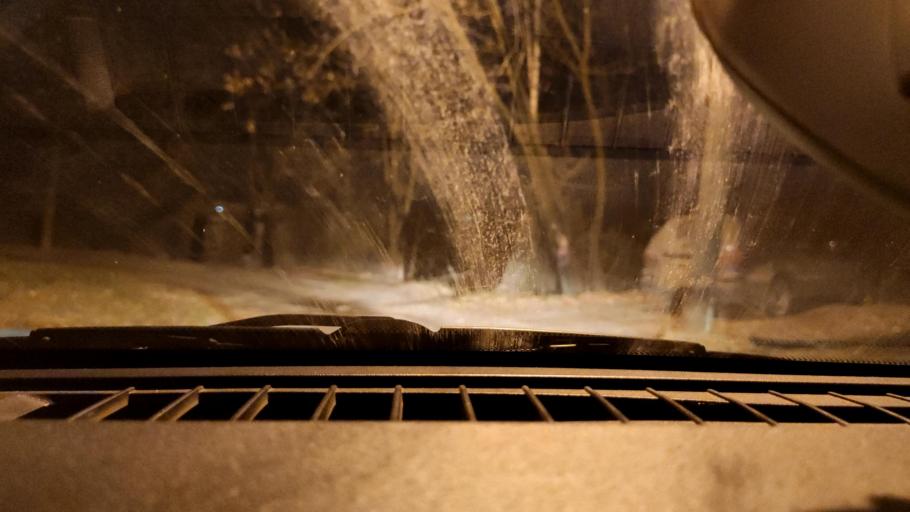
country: RU
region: Perm
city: Perm
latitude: 57.9594
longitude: 56.2221
